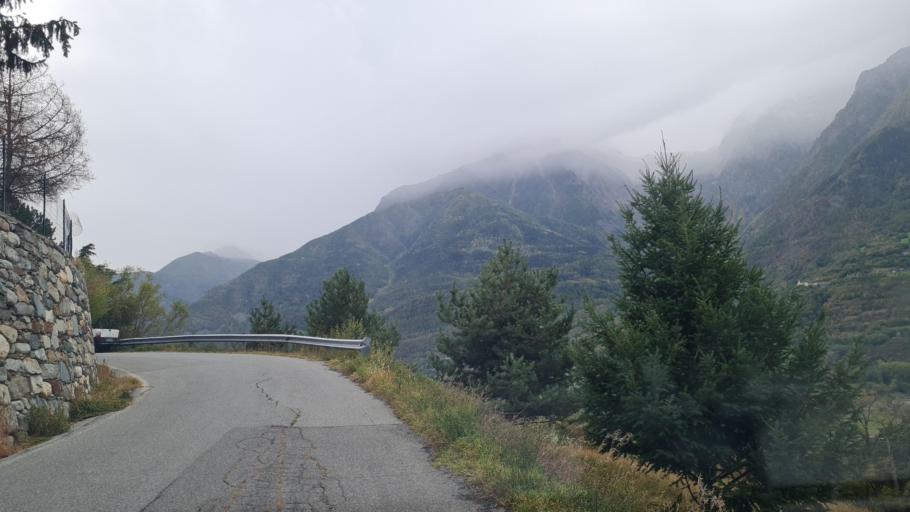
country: IT
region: Aosta Valley
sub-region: Valle d'Aosta
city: Quart
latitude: 45.7453
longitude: 7.4084
